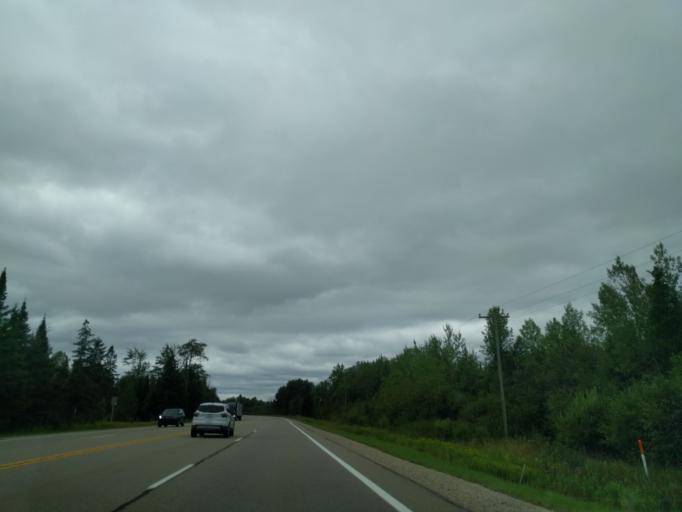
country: US
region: Michigan
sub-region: Delta County
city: Escanaba
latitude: 45.5356
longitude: -87.2835
